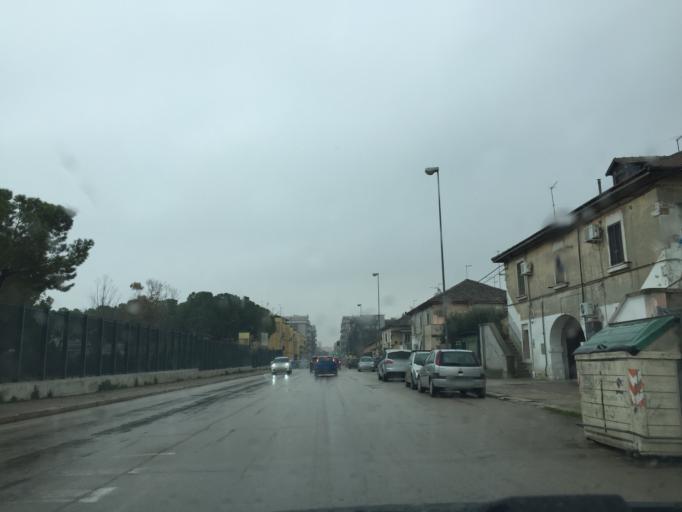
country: IT
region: Apulia
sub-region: Provincia di Foggia
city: Foggia
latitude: 41.4675
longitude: 15.5275
